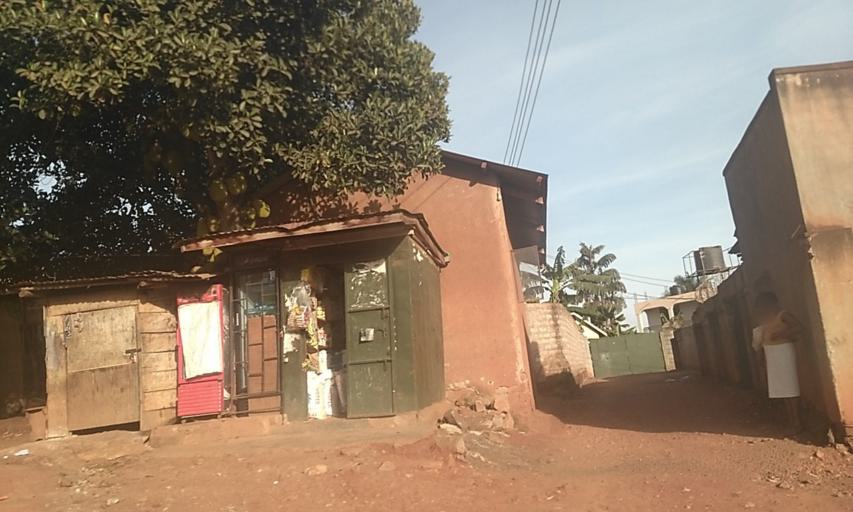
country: UG
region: Central Region
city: Kampala Central Division
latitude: 0.3608
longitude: 32.5987
